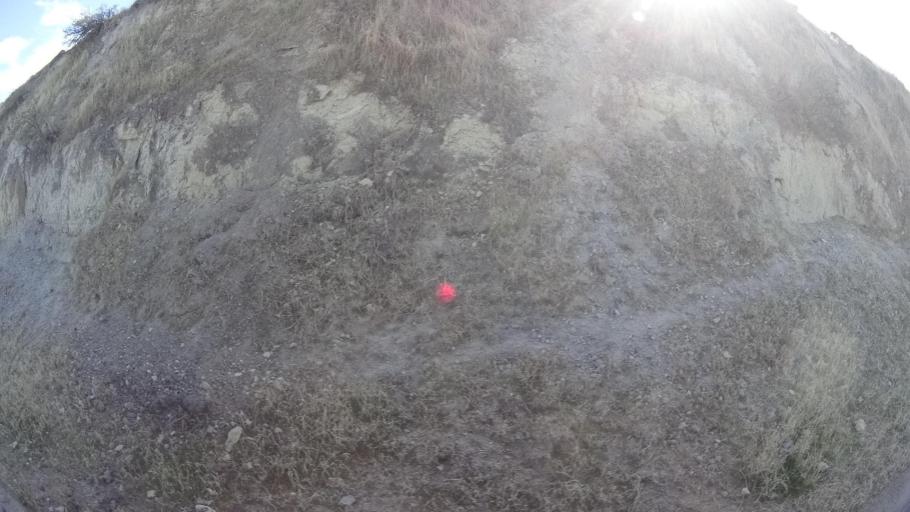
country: US
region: California
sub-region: Kern County
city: Oildale
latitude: 35.4967
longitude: -118.8646
